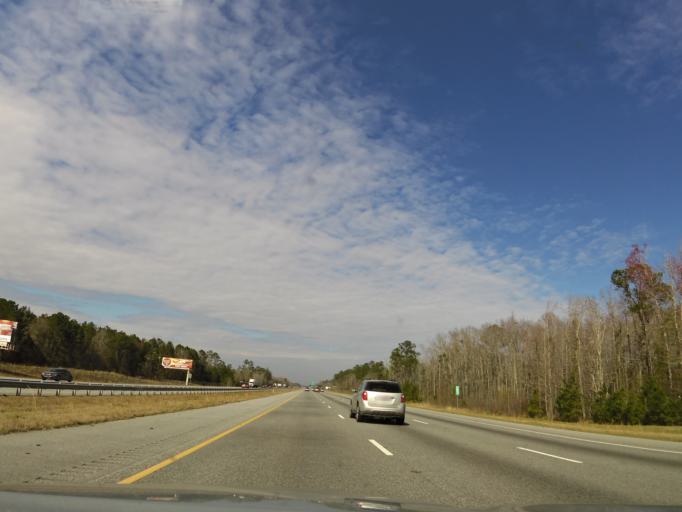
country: US
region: Georgia
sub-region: McIntosh County
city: Darien
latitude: 31.5133
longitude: -81.4458
